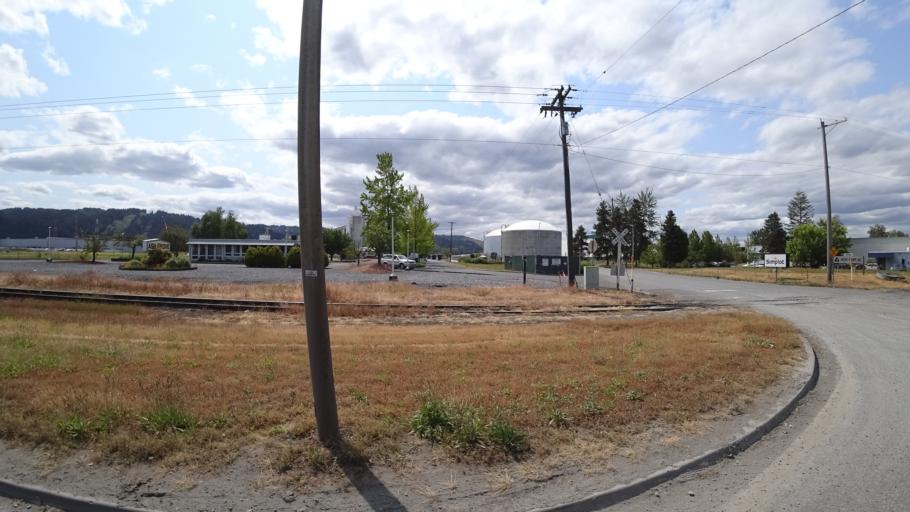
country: US
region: Oregon
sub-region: Washington County
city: Oak Hills
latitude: 45.6236
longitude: -122.7802
